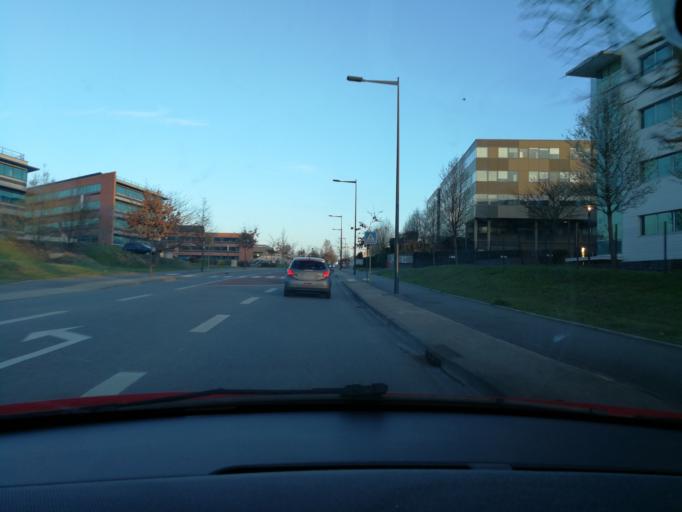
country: FR
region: Midi-Pyrenees
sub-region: Departement de la Haute-Garonne
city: Balma
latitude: 43.6293
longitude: 1.4892
